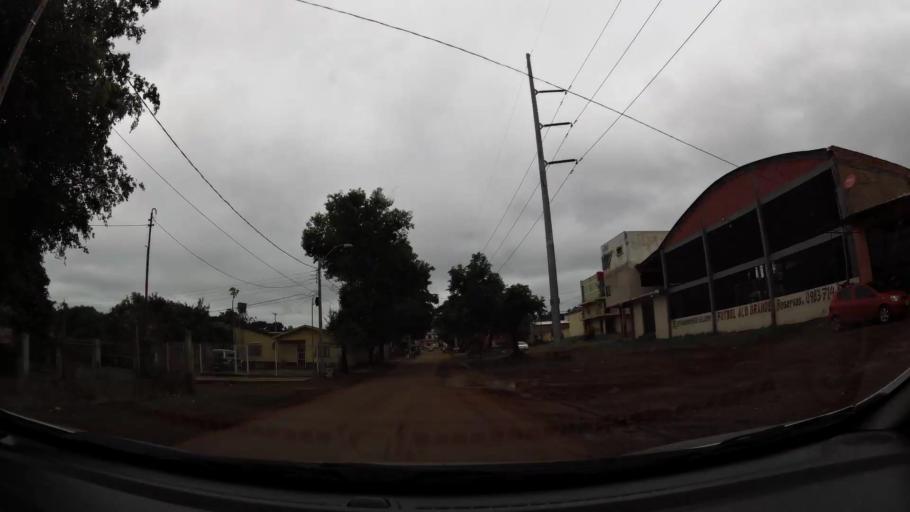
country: PY
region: Alto Parana
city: Presidente Franco
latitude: -25.5152
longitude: -54.6752
